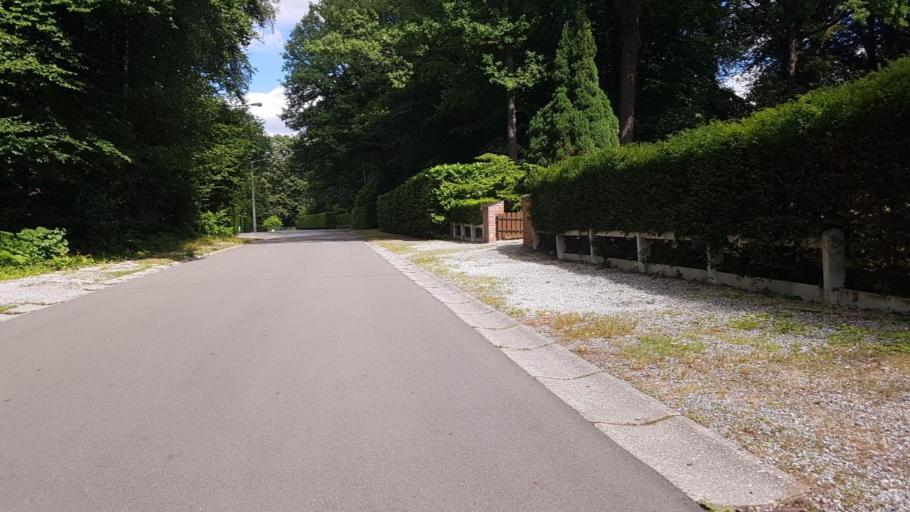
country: BE
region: Wallonia
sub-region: Province du Hainaut
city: Charleroi
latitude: 50.3544
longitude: 4.4371
